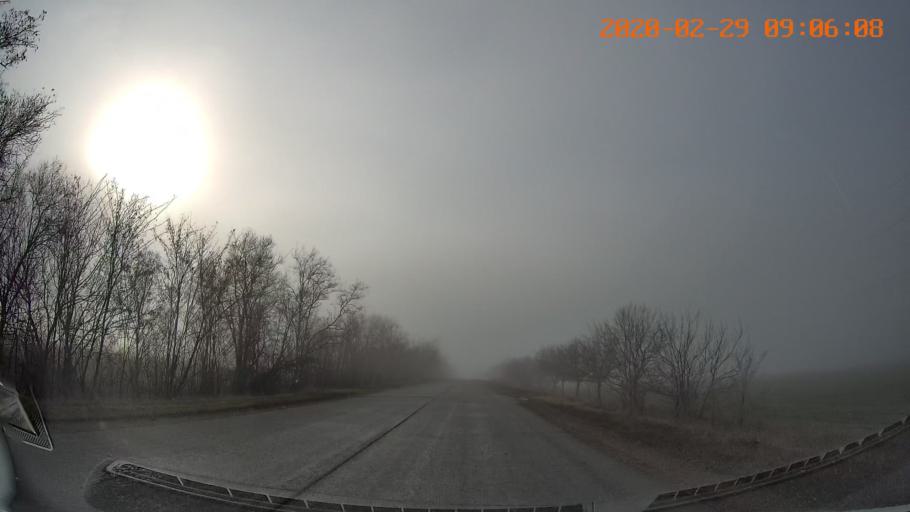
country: MD
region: Telenesti
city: Tiraspolul Nou
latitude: 46.8797
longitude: 29.7433
